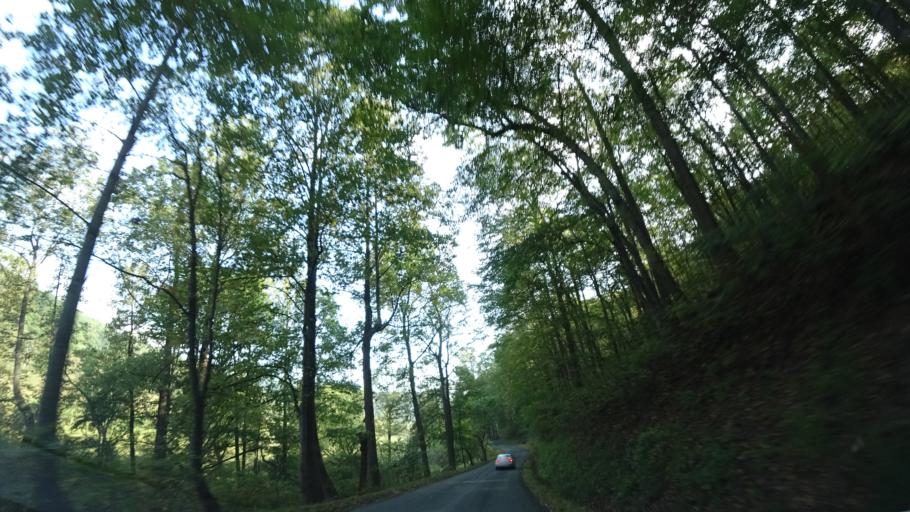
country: US
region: Virginia
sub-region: Madison County
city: Madison
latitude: 38.5092
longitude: -78.3108
